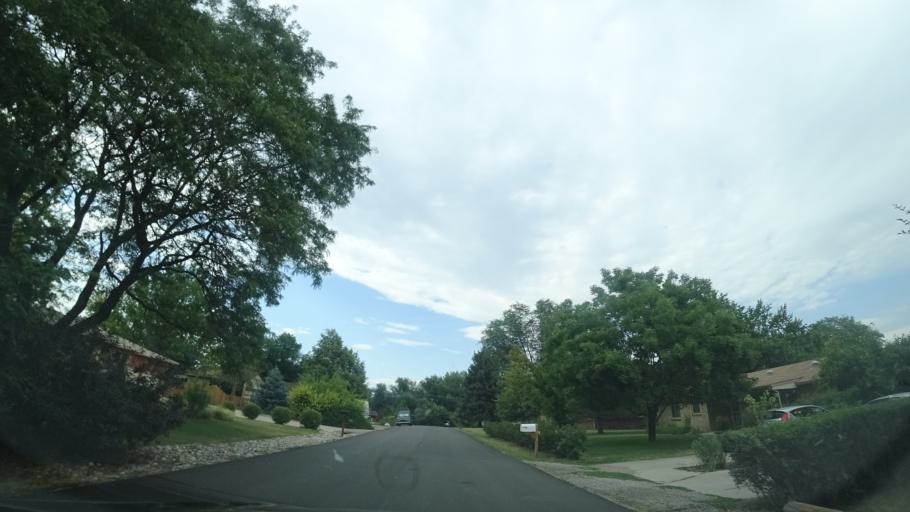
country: US
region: Colorado
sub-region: Jefferson County
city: Lakewood
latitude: 39.7174
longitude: -105.0850
